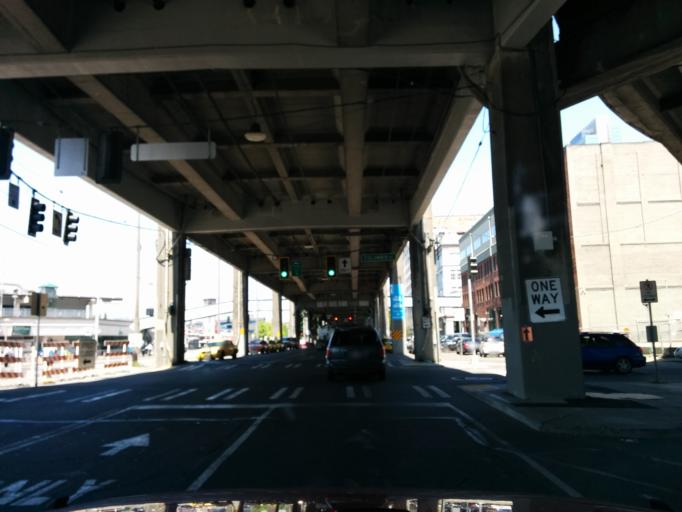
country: US
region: Washington
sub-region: King County
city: Seattle
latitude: 47.6022
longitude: -122.3366
